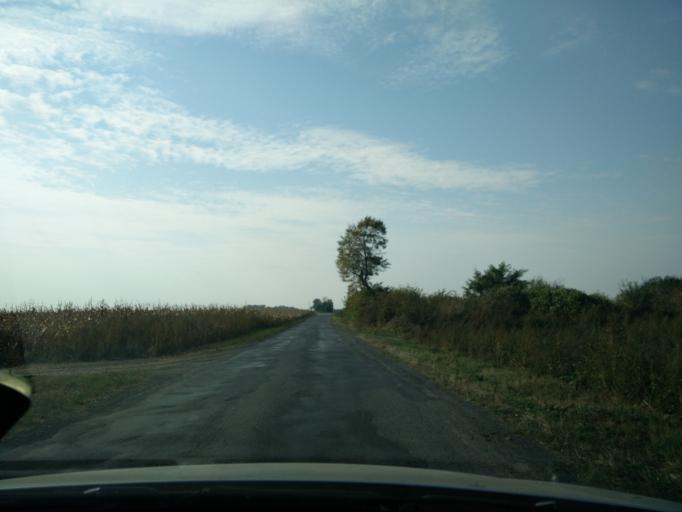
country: PL
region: Greater Poland Voivodeship
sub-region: Powiat sredzki
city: Dominowo
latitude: 52.3131
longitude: 17.3109
